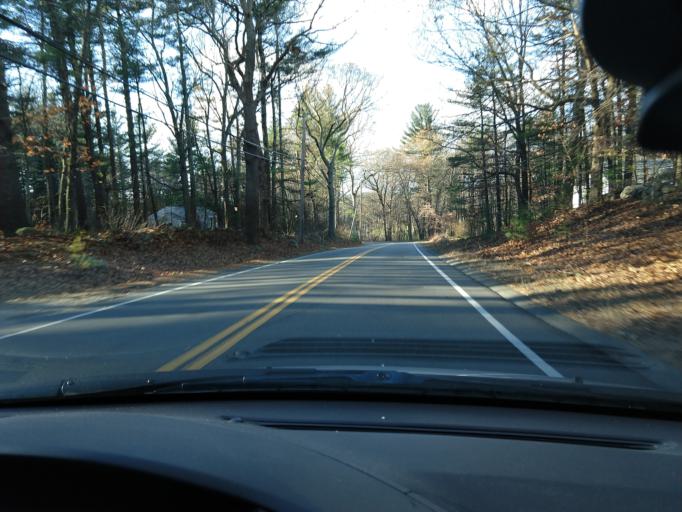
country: US
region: Massachusetts
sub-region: Middlesex County
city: Westford
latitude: 42.5461
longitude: -71.4099
